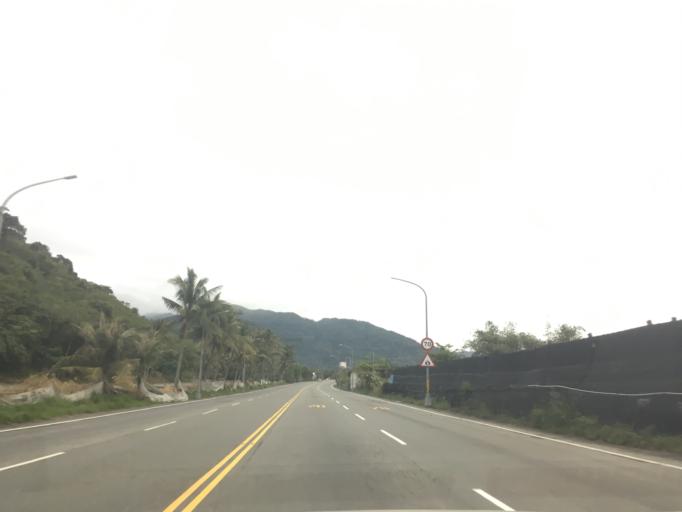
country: TW
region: Taiwan
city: Taitung City
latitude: 22.7424
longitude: 121.0573
